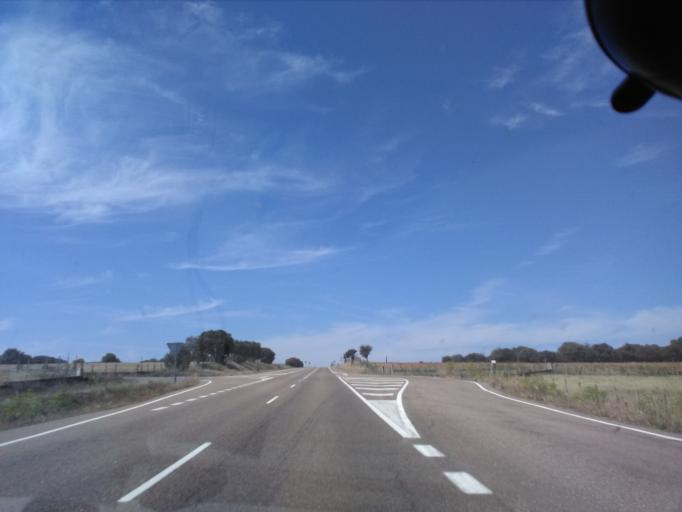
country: ES
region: Castille and Leon
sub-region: Provincia de Salamanca
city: Miranda de Azan
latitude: 40.8698
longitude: -5.7564
